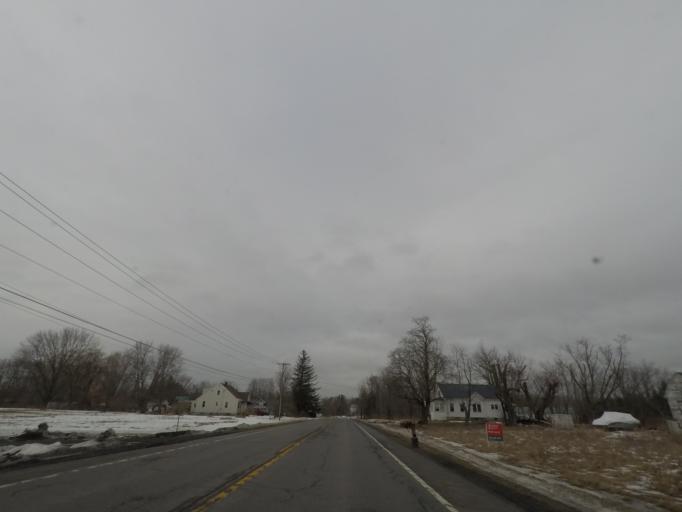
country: US
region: New York
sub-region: Schenectady County
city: Rotterdam
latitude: 42.7500
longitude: -73.9842
